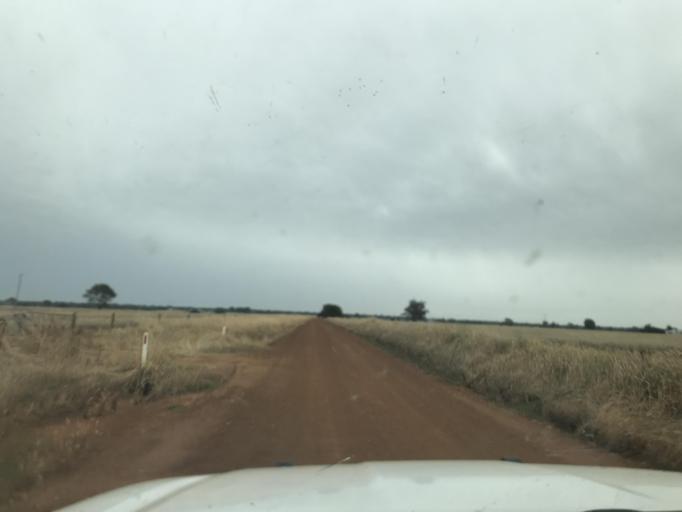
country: AU
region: Victoria
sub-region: Horsham
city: Horsham
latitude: -37.0606
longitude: 141.6114
